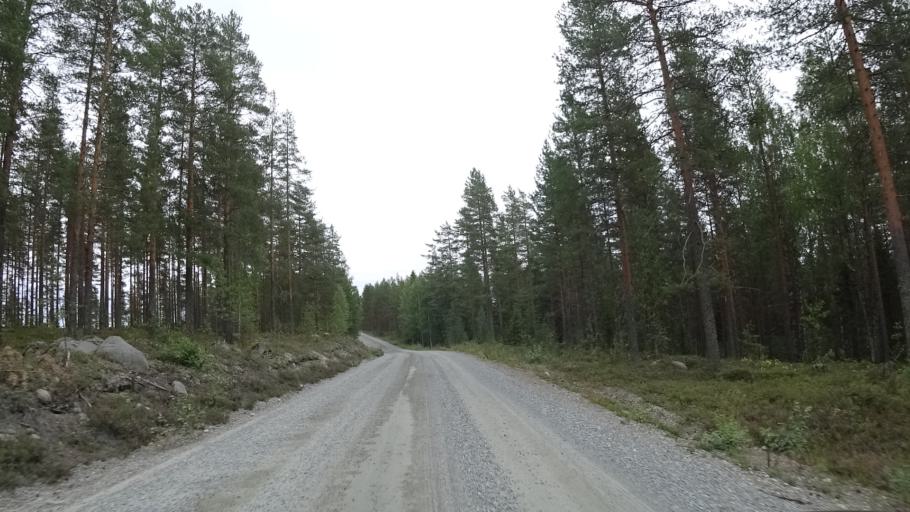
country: FI
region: North Karelia
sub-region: Pielisen Karjala
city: Lieksa
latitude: 63.3703
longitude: 30.3793
